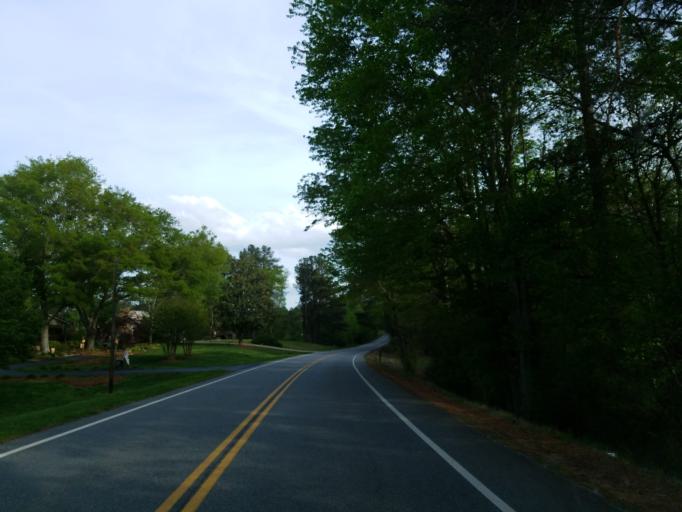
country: US
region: Georgia
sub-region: Pickens County
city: Nelson
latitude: 34.3525
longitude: -84.2674
